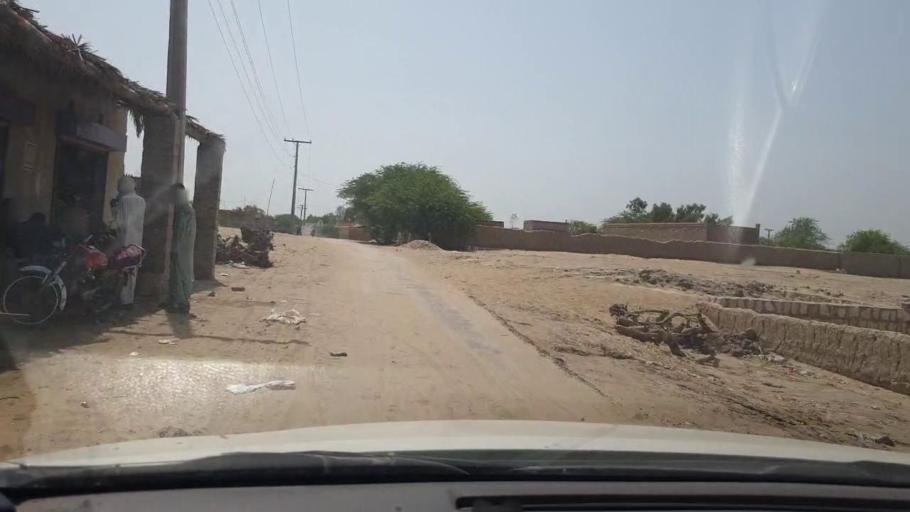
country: PK
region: Sindh
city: Rohri
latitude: 27.5219
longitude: 69.0552
